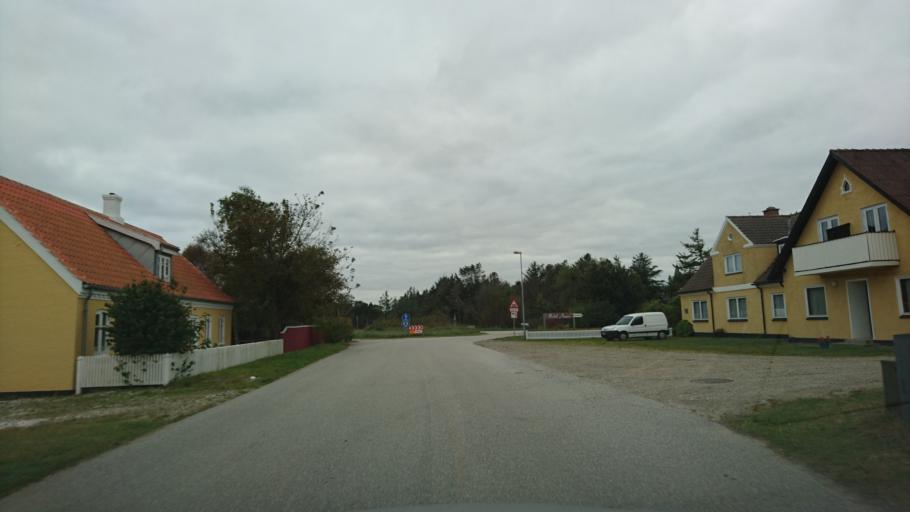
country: DK
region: North Denmark
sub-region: Frederikshavn Kommune
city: Skagen
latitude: 57.6587
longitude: 10.4618
